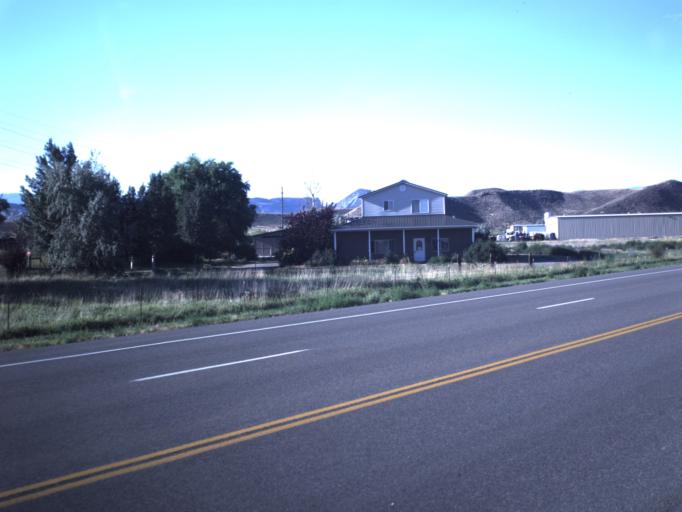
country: US
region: Utah
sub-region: Sevier County
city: Salina
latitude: 38.9492
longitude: -111.8788
